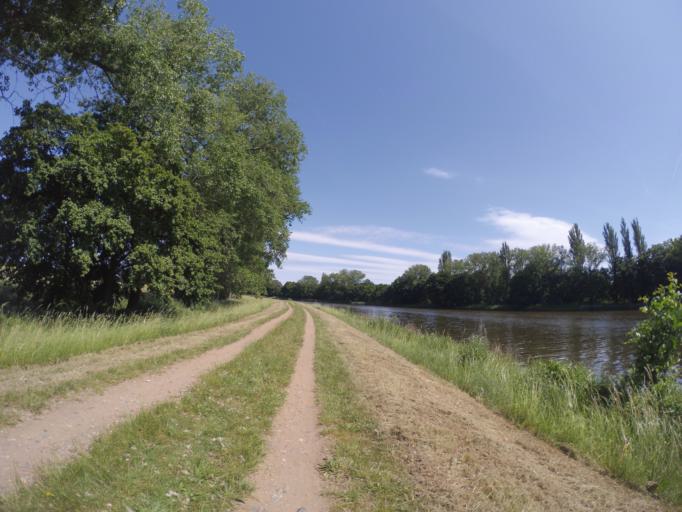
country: CZ
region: Central Bohemia
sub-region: Okres Nymburk
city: Sadska
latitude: 50.1696
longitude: 14.9949
